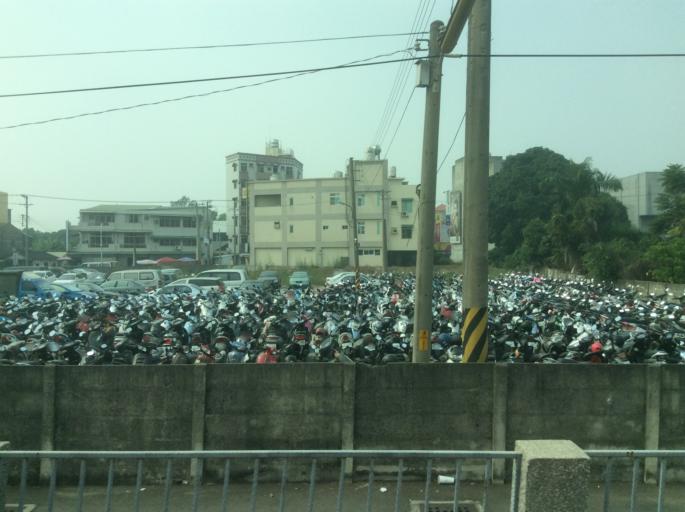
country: TW
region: Taiwan
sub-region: Chiayi
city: Jiayi Shi
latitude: 23.5538
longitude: 120.4310
